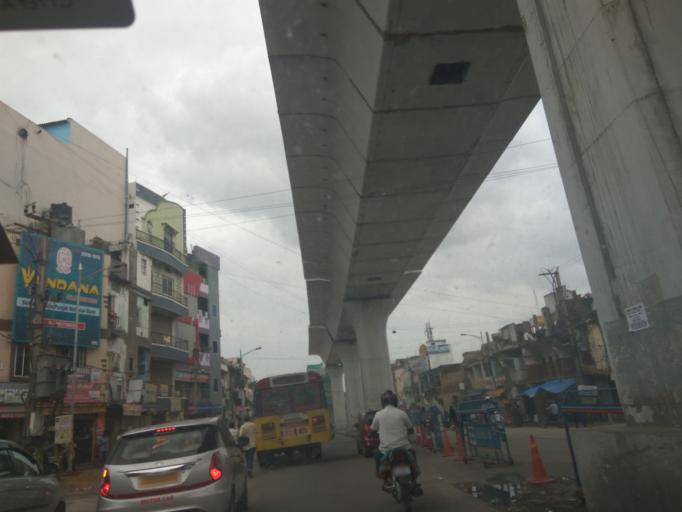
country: IN
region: Telangana
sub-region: Hyderabad
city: Hyderabad
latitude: 17.4025
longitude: 78.4951
